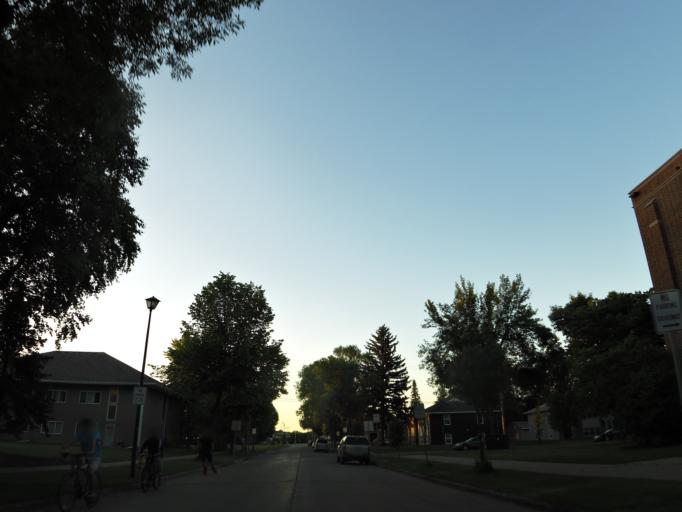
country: US
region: North Dakota
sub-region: Grand Forks County
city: Grand Forks
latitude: 47.9238
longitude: -97.0755
